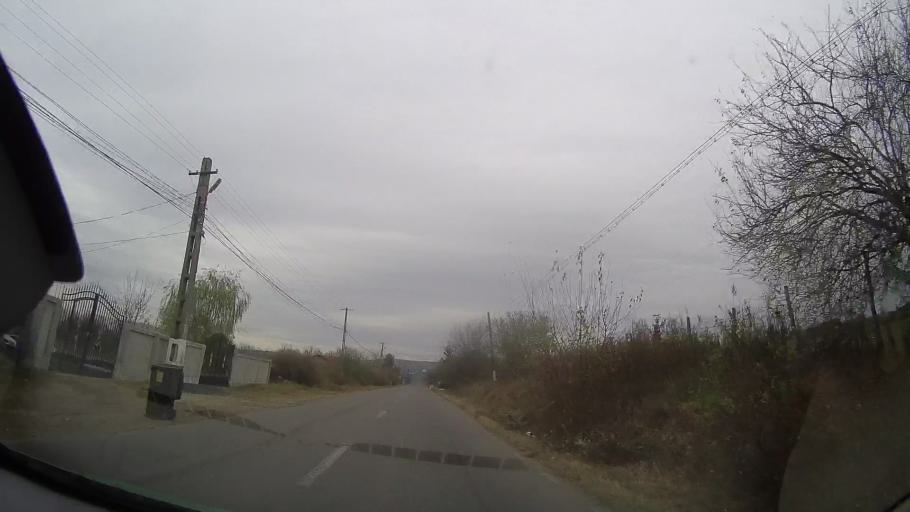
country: RO
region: Prahova
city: Mocesti
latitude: 45.0638
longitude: 26.2478
